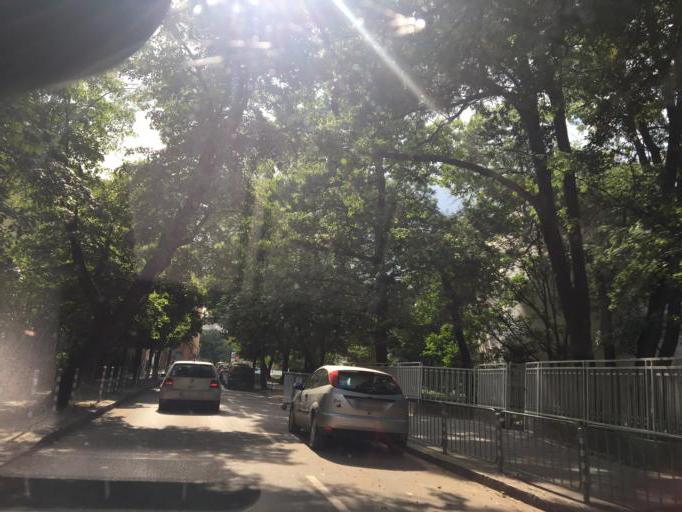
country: BG
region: Sofia-Capital
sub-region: Stolichna Obshtina
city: Sofia
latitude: 42.6825
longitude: 23.3323
